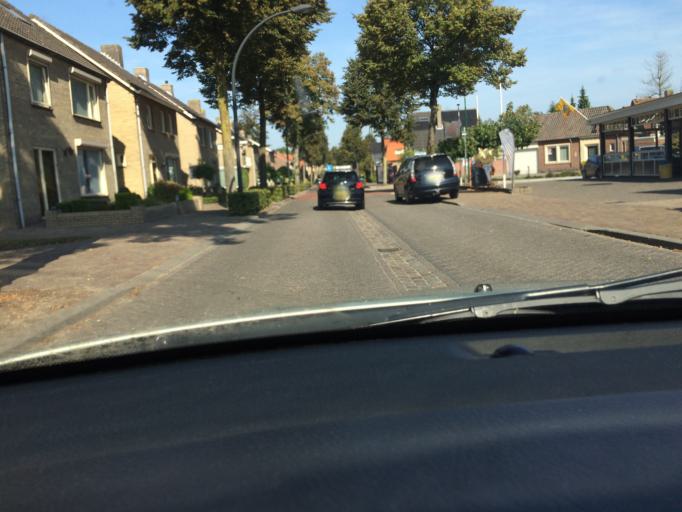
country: NL
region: North Brabant
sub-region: Gemeente Baarle-Nassau
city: Baarle-Nassau
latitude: 51.4791
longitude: 4.9549
